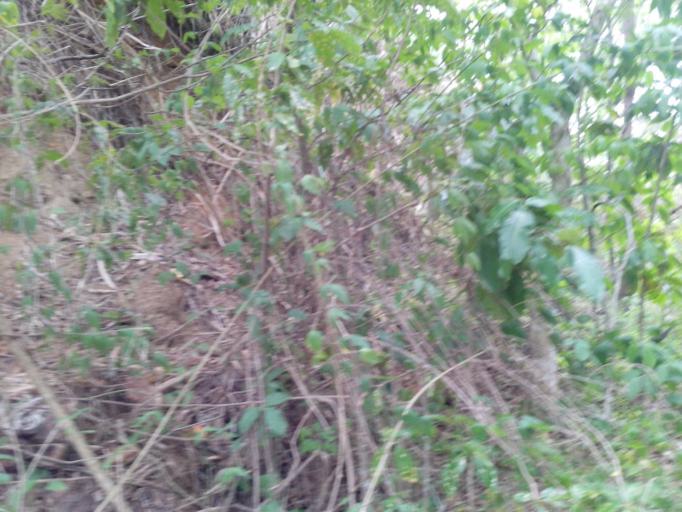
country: BR
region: Rio de Janeiro
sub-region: Miguel Pereira
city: Miguel Pereira
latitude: -22.5092
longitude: -43.5178
